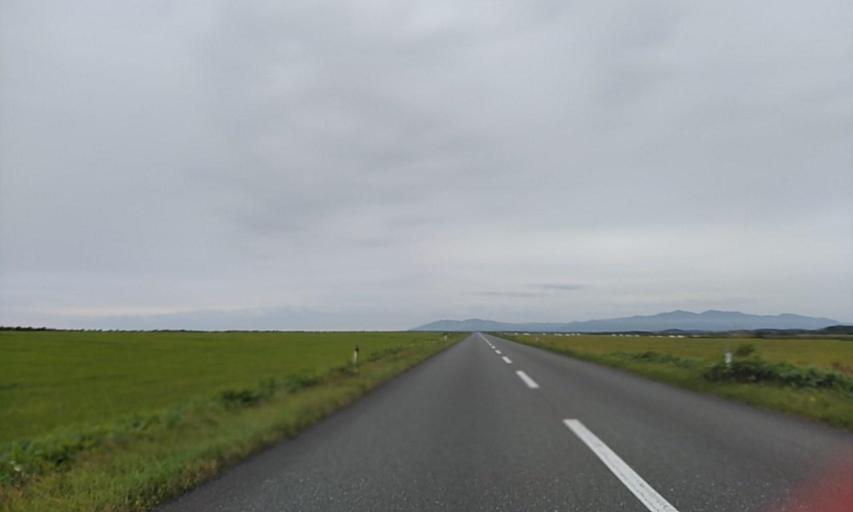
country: JP
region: Hokkaido
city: Makubetsu
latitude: 45.2042
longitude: 142.2963
